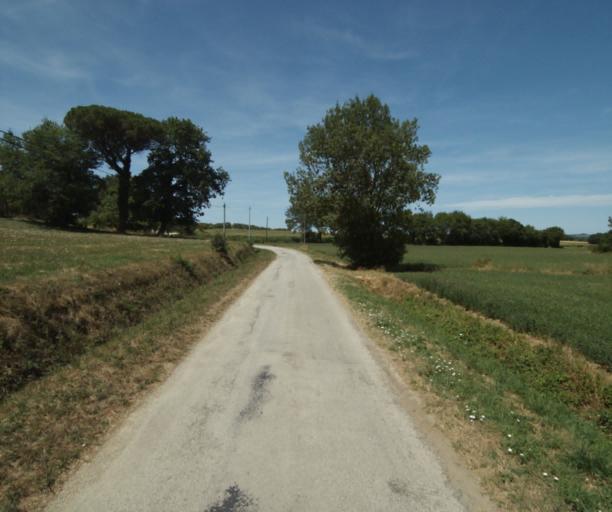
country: FR
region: Midi-Pyrenees
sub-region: Departement de la Haute-Garonne
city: Revel
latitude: 43.4940
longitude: 2.0179
